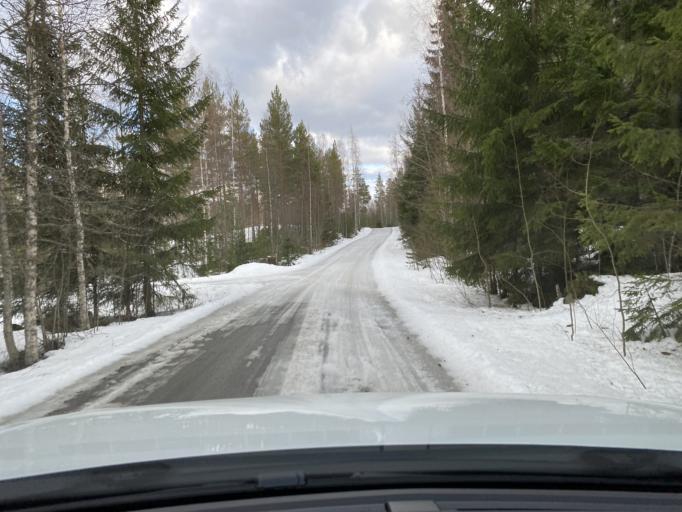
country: FI
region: Pirkanmaa
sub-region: Lounais-Pirkanmaa
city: Mouhijaervi
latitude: 61.4324
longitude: 22.9883
